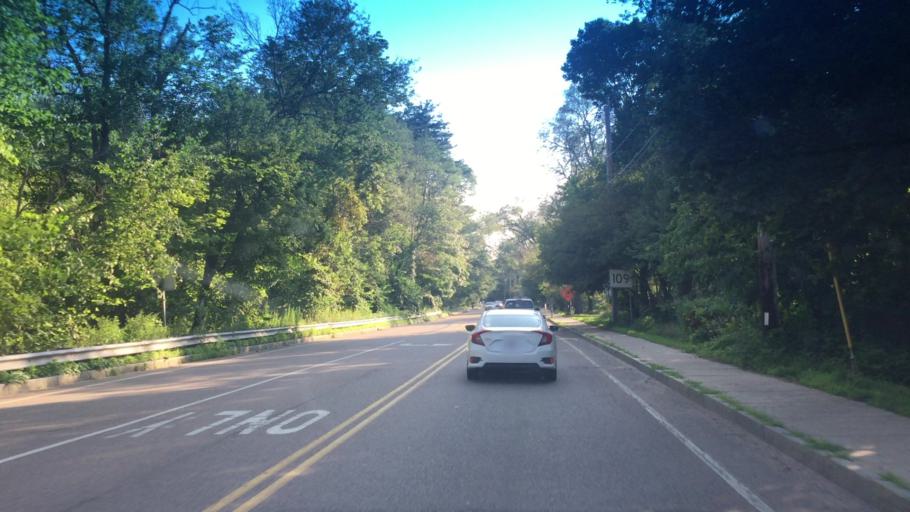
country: US
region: Massachusetts
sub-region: Norfolk County
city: Millis-Clicquot
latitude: 42.1769
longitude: -71.3346
